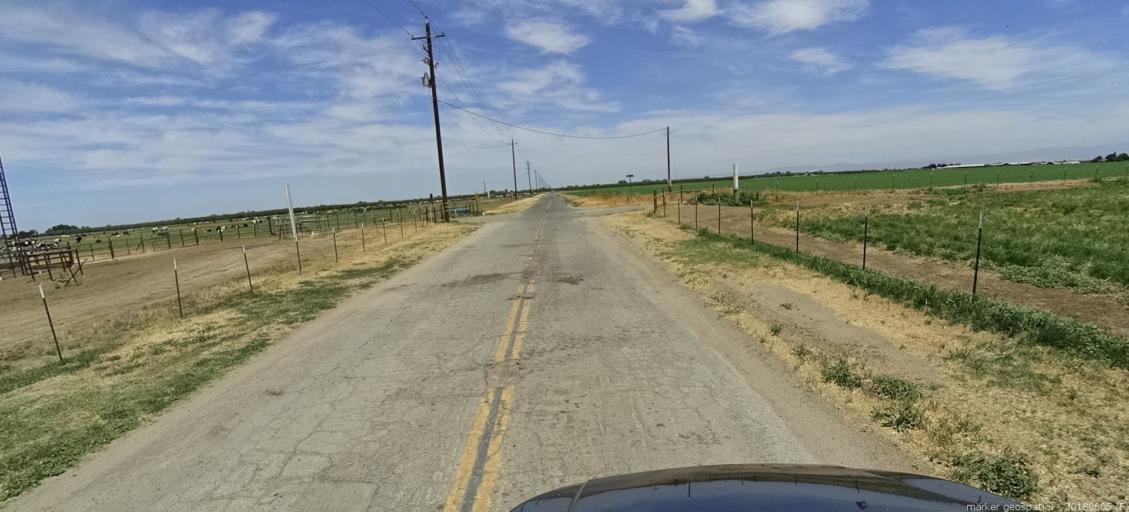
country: US
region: California
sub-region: Madera County
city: Chowchilla
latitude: 37.0977
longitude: -120.3290
